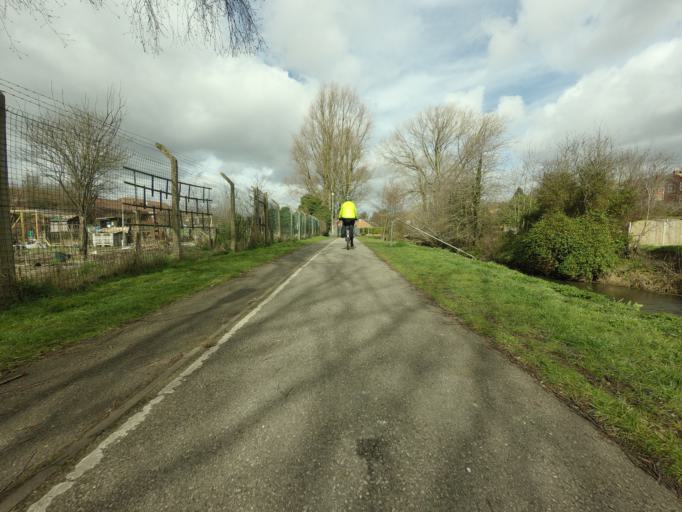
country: GB
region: England
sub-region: Lincolnshire
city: Grantham
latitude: 52.9066
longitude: -0.6346
